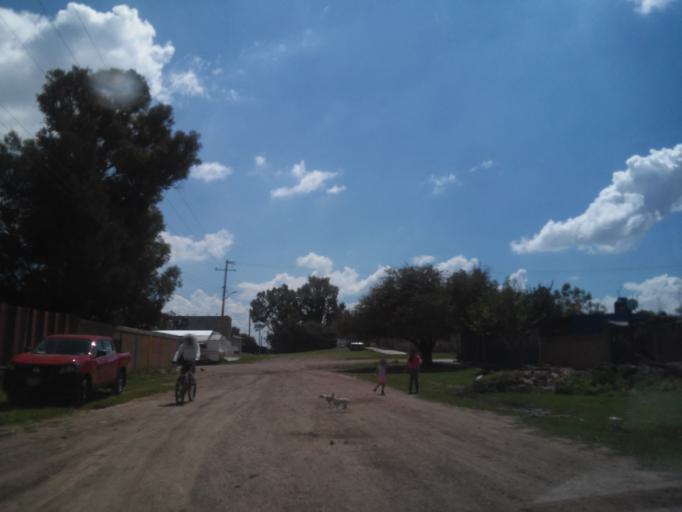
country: MX
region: Durango
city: Victoria de Durango
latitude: 24.0126
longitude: -104.7395
